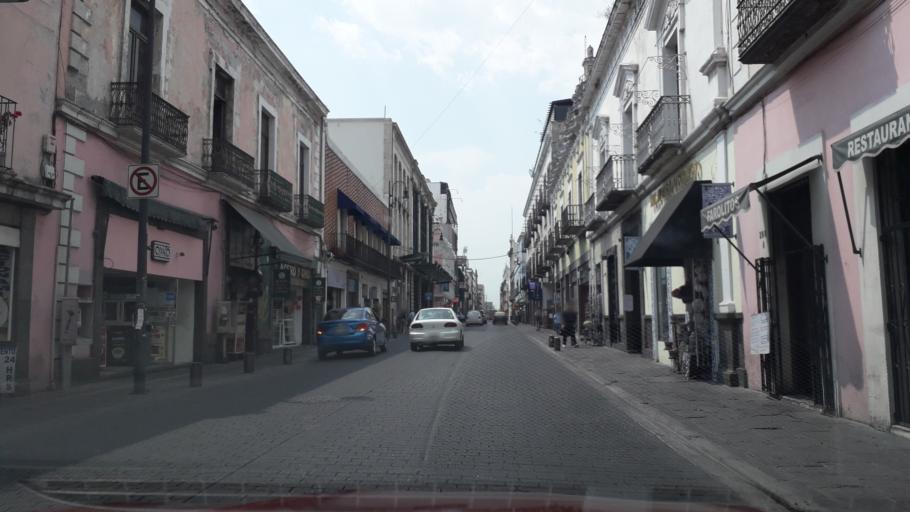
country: MX
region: Puebla
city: Puebla
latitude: 19.0439
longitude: -98.1958
